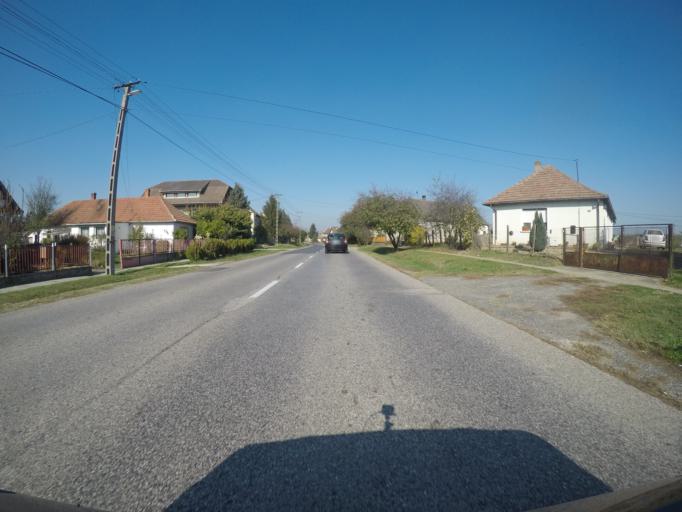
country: HU
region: Tolna
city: Szedres
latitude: 46.4804
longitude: 18.6832
